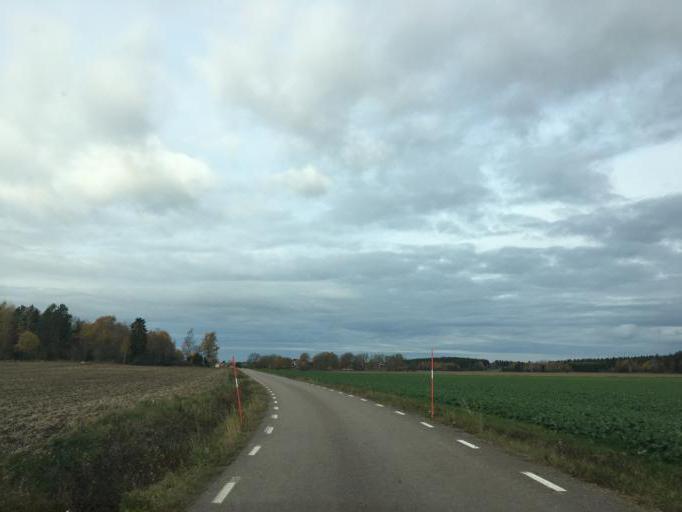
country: SE
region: Soedermanland
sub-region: Eskilstuna Kommun
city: Kvicksund
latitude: 59.5442
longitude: 16.3627
